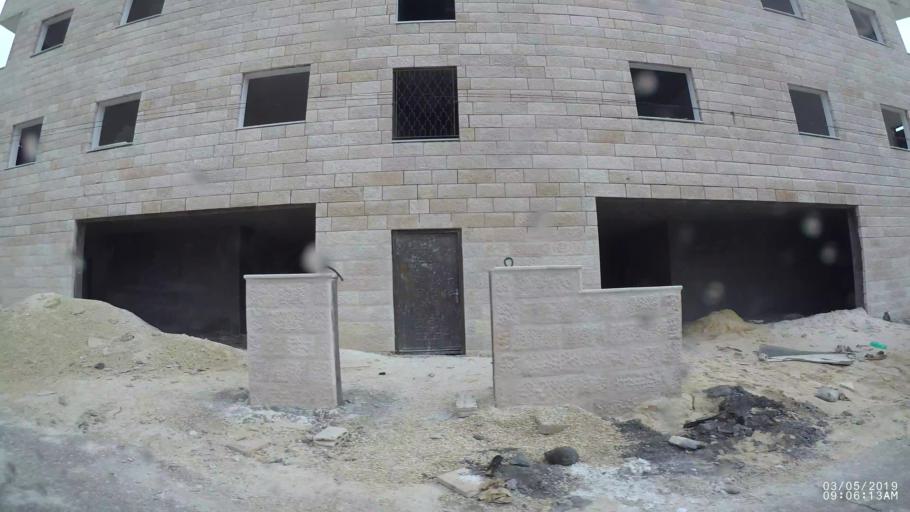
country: JO
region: Amman
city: Amman
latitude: 31.9596
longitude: 35.9411
